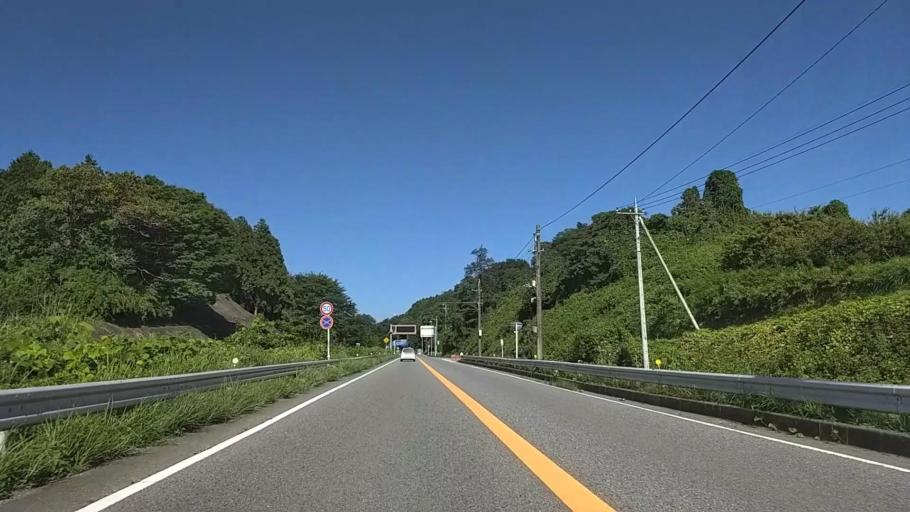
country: JP
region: Gunma
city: Annaka
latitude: 36.3153
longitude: 138.8053
